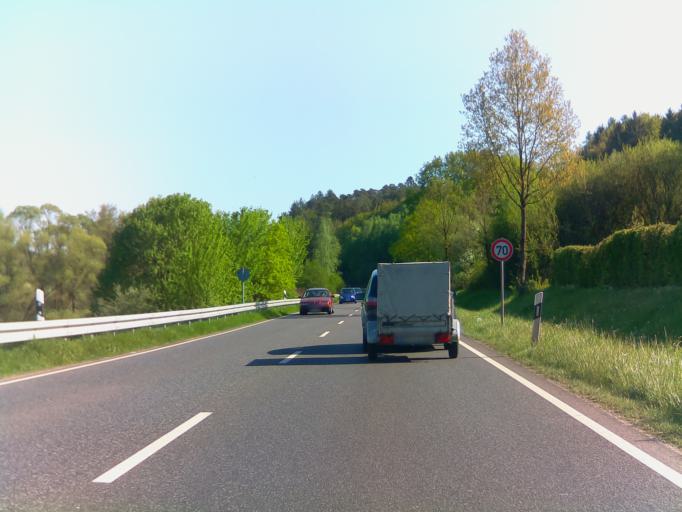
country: DE
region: Hesse
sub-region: Regierungsbezirk Darmstadt
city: Wachtersbach
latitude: 50.2971
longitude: 9.3005
